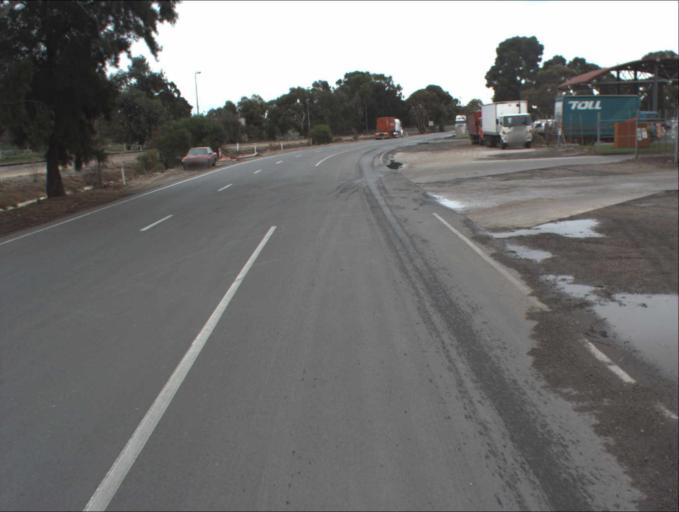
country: AU
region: South Australia
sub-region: Prospect
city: Prospect
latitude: -34.8715
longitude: 138.5781
